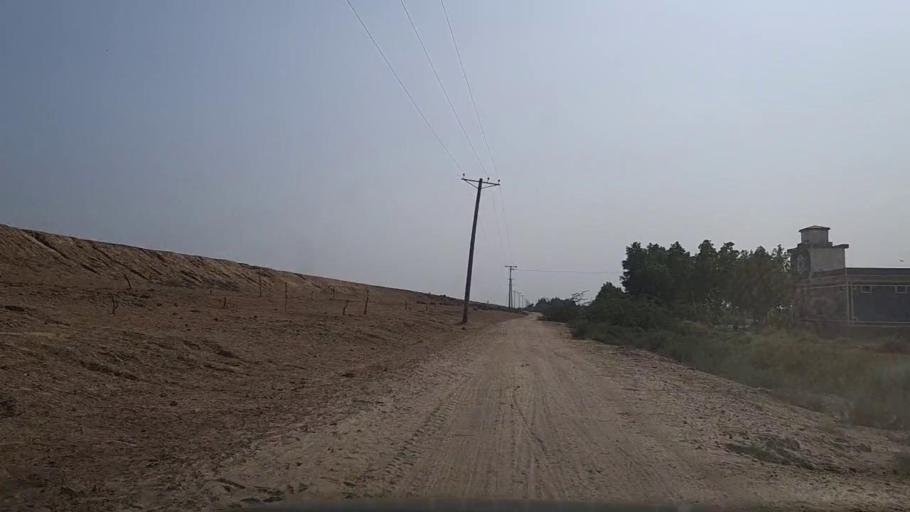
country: PK
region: Sindh
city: Chuhar Jamali
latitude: 24.5579
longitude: 67.9154
